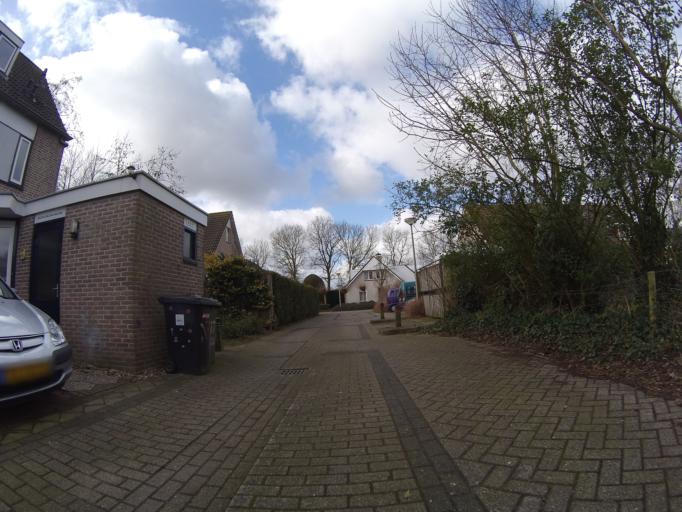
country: NL
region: Gelderland
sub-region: Gemeente Barneveld
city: Zwartebroek
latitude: 52.1799
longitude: 5.4573
